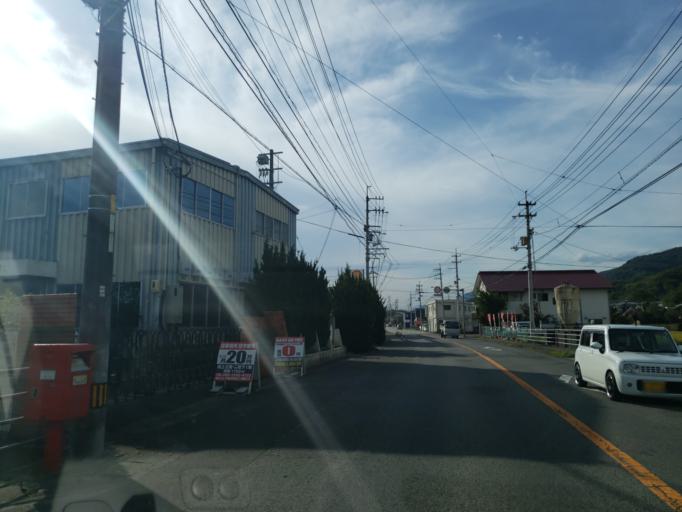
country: JP
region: Tokushima
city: Wakimachi
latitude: 34.0704
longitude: 134.1396
